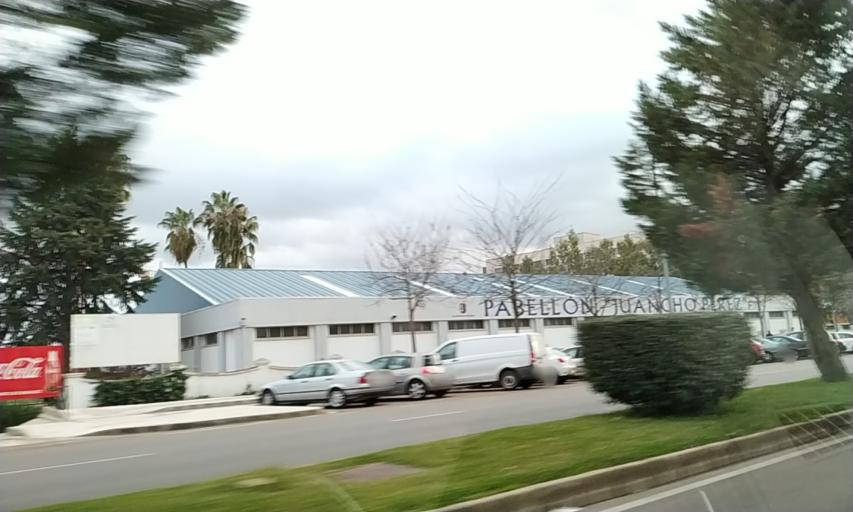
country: ES
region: Extremadura
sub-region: Provincia de Badajoz
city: Badajoz
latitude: 38.8849
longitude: -6.9823
